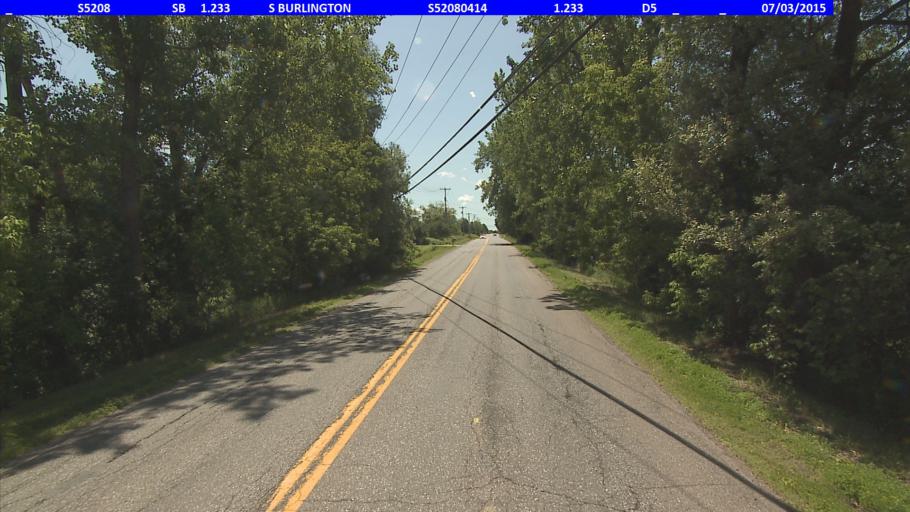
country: US
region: Vermont
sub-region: Chittenden County
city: South Burlington
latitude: 44.4285
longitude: -73.1747
